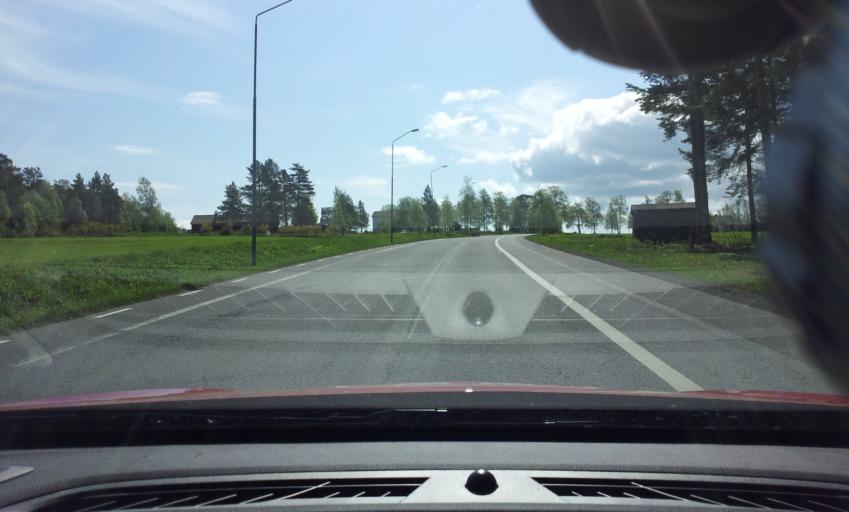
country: SE
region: Jaemtland
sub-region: OEstersunds Kommun
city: Ostersund
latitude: 63.1874
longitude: 14.5022
